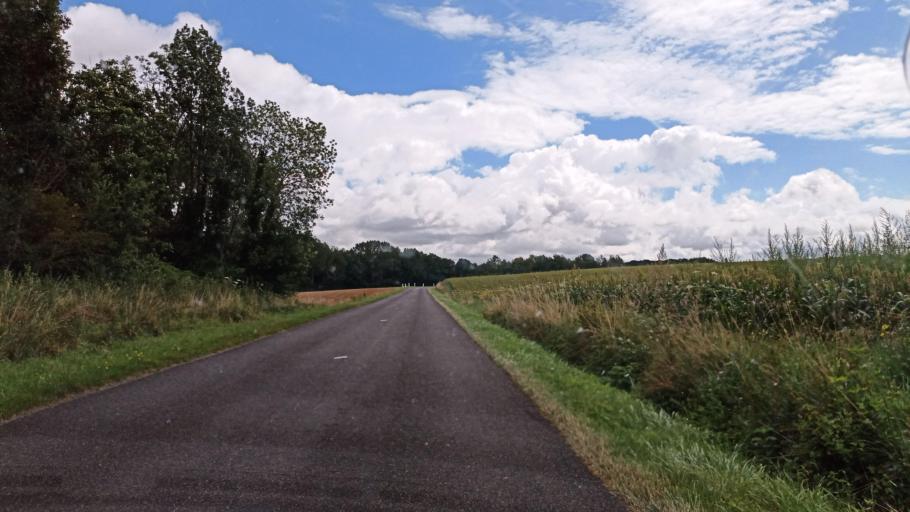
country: FR
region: Ile-de-France
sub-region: Departement de Seine-et-Marne
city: Voulx
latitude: 48.2603
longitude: 3.0135
